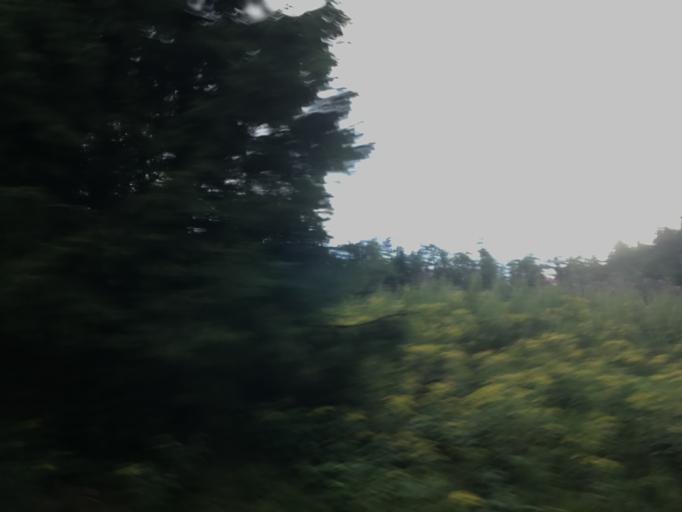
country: DE
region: Lower Saxony
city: Sankt Andreasberg
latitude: 51.7532
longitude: 10.5198
